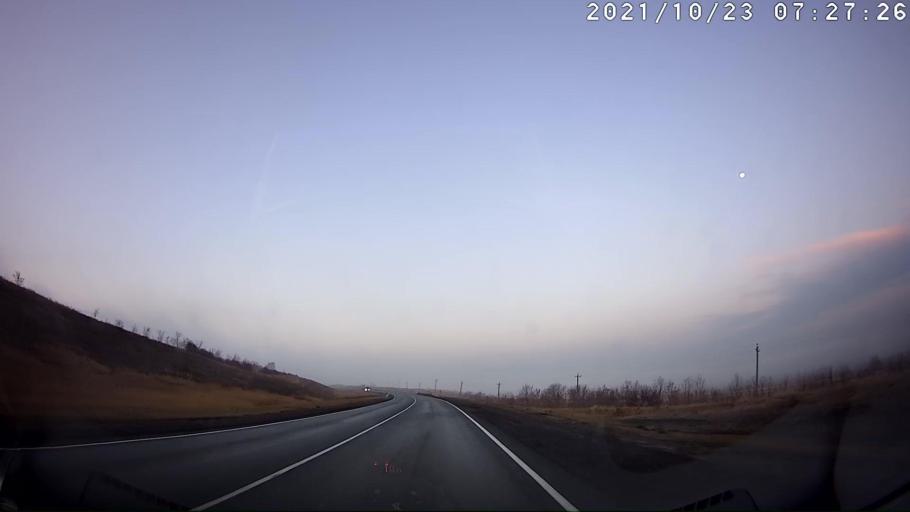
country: RU
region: Saratov
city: Alekseyevka
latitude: 52.3340
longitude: 47.9257
